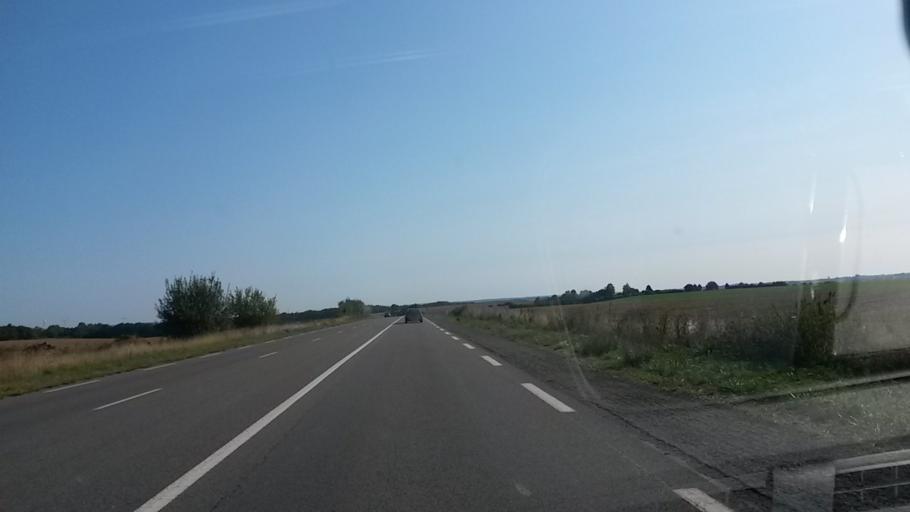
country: FR
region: Picardie
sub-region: Departement de l'Aisne
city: Guise
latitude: 49.8861
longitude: 3.6130
